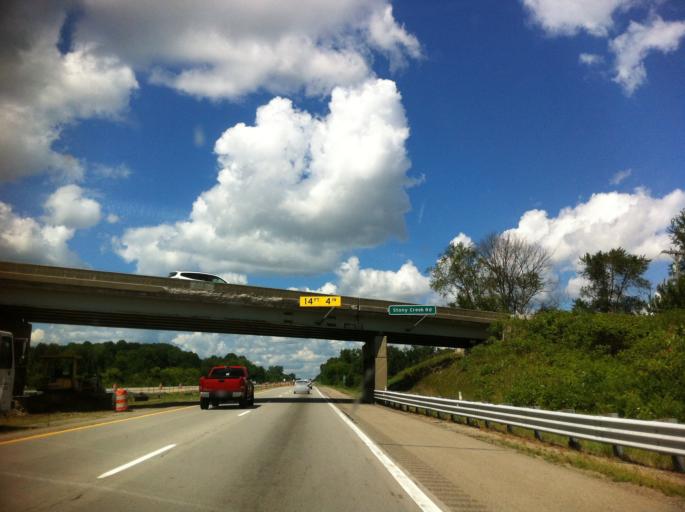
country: US
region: Michigan
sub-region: Washtenaw County
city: Milan
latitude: 42.1313
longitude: -83.6829
